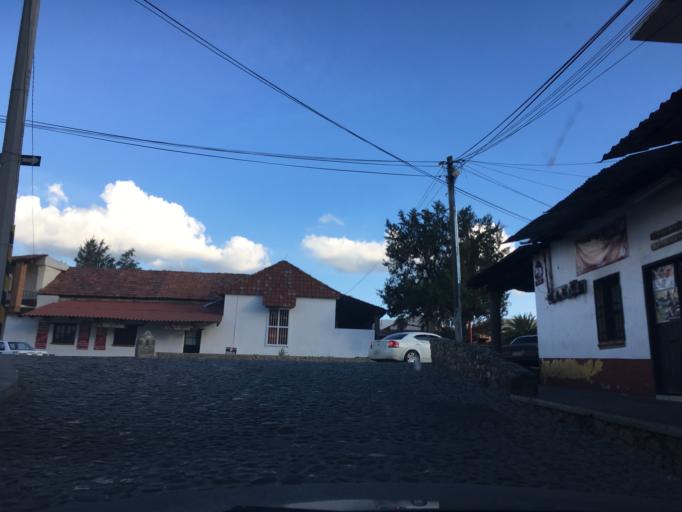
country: MX
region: Hidalgo
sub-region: Omitlan de Juarez
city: San Antonio el Paso
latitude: 20.2044
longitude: -98.5752
